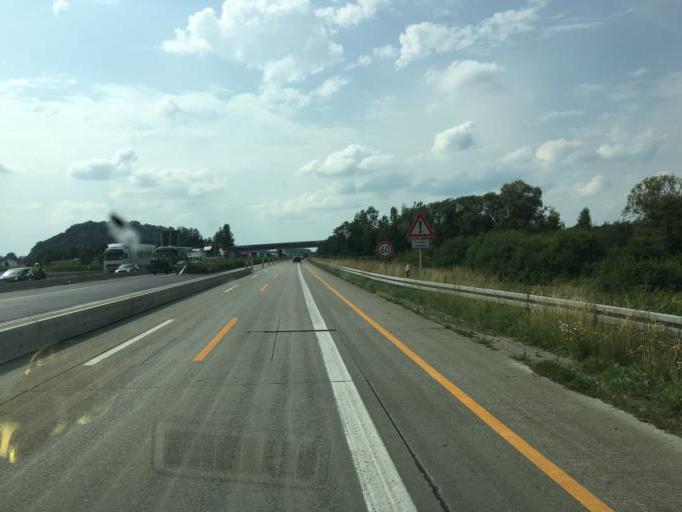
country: DE
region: Bavaria
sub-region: Lower Bavaria
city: Deggendorf
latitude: 48.8220
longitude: 12.9300
